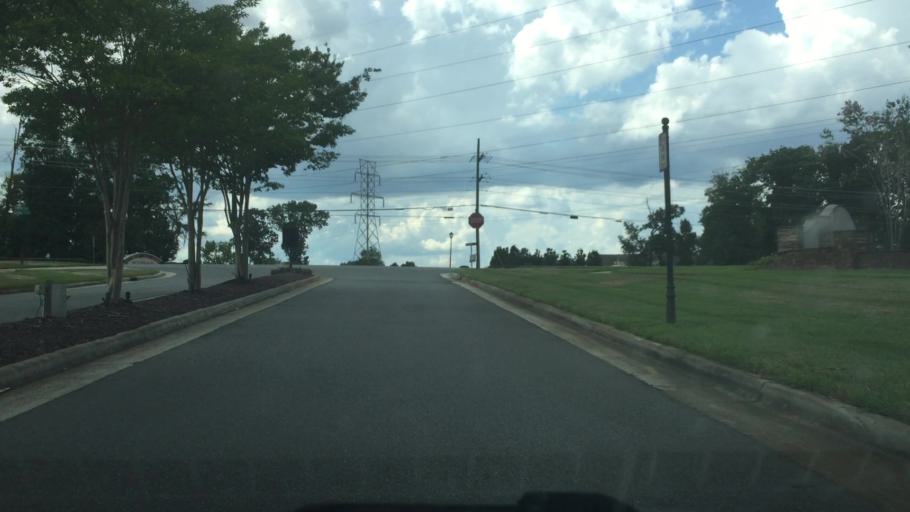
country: US
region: North Carolina
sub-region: Mecklenburg County
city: Huntersville
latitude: 35.4053
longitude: -80.7557
